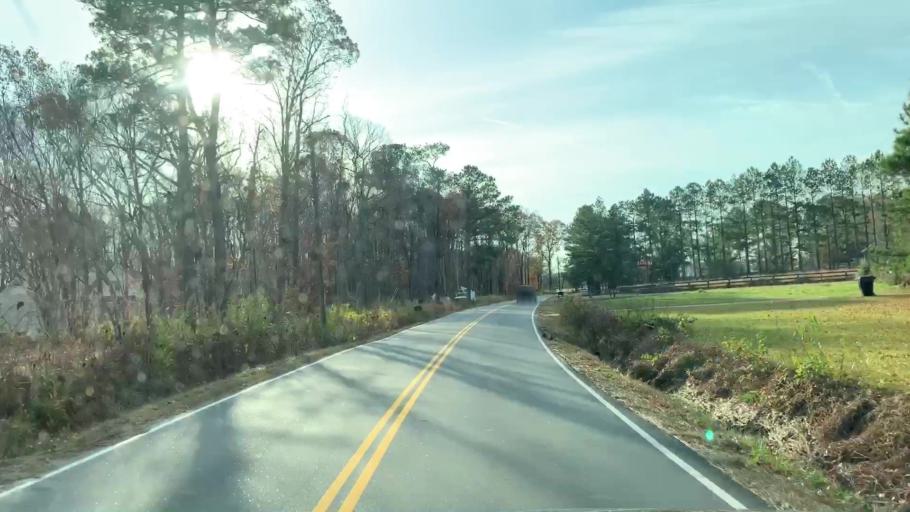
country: US
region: Virginia
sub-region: City of Virginia Beach
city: Virginia Beach
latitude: 36.7128
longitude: -76.0488
